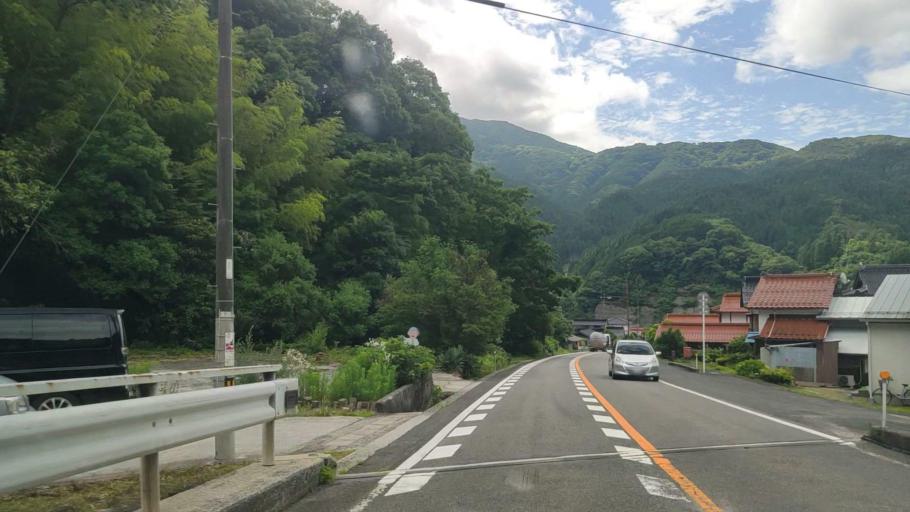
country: JP
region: Tottori
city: Yonago
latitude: 35.2467
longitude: 133.4439
